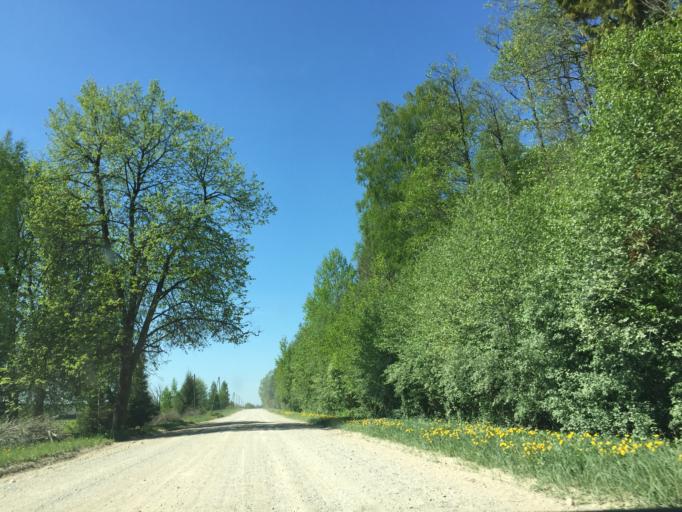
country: LV
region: Kegums
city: Kegums
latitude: 56.8652
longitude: 24.7685
